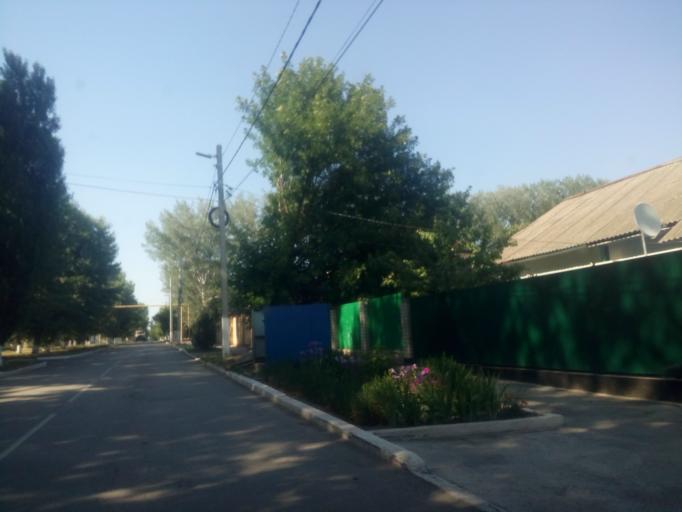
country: RU
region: Rostov
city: Sholokhovskiy
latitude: 48.2803
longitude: 41.0378
